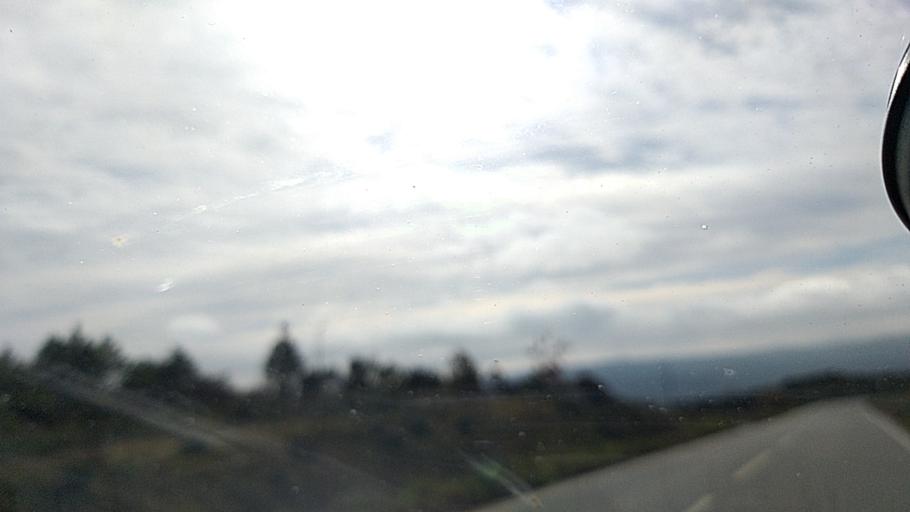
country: PT
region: Guarda
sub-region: Aguiar da Beira
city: Aguiar da Beira
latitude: 40.7537
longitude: -7.5440
